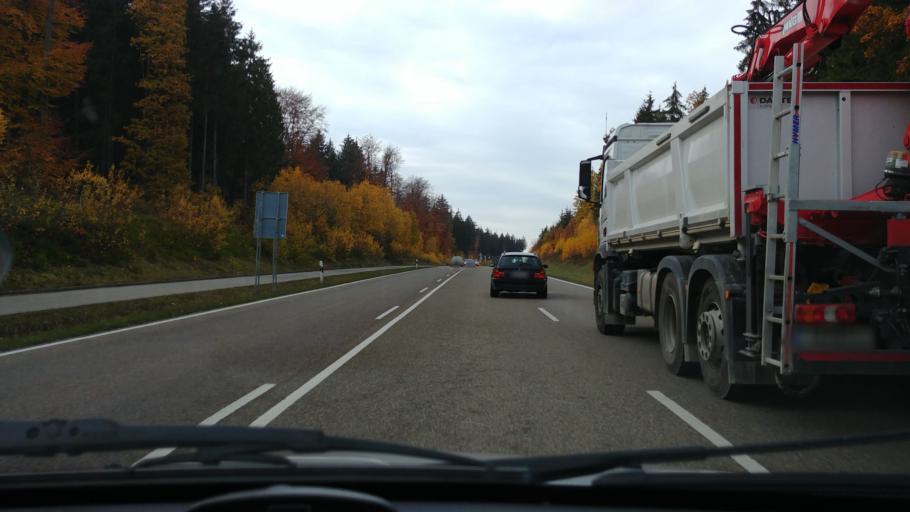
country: DE
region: Baden-Wuerttemberg
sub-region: Regierungsbezirk Stuttgart
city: Nattheim
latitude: 48.6622
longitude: 10.2649
